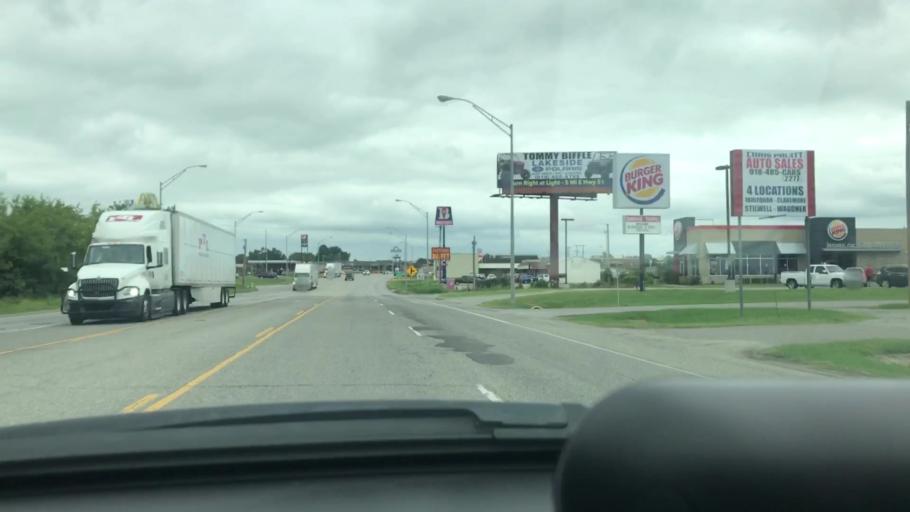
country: US
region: Oklahoma
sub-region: Wagoner County
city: Wagoner
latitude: 35.9552
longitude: -95.3952
